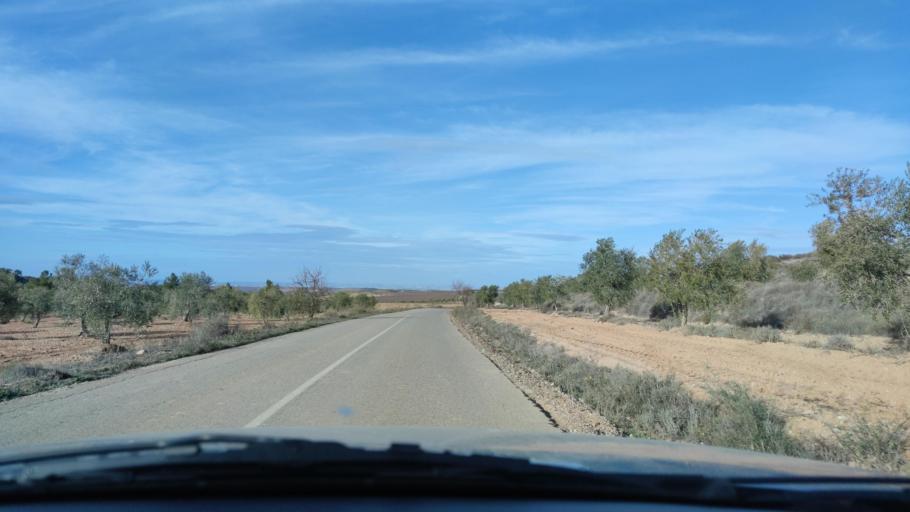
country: ES
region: Catalonia
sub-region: Provincia de Lleida
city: el Cogul
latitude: 41.4669
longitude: 0.6725
